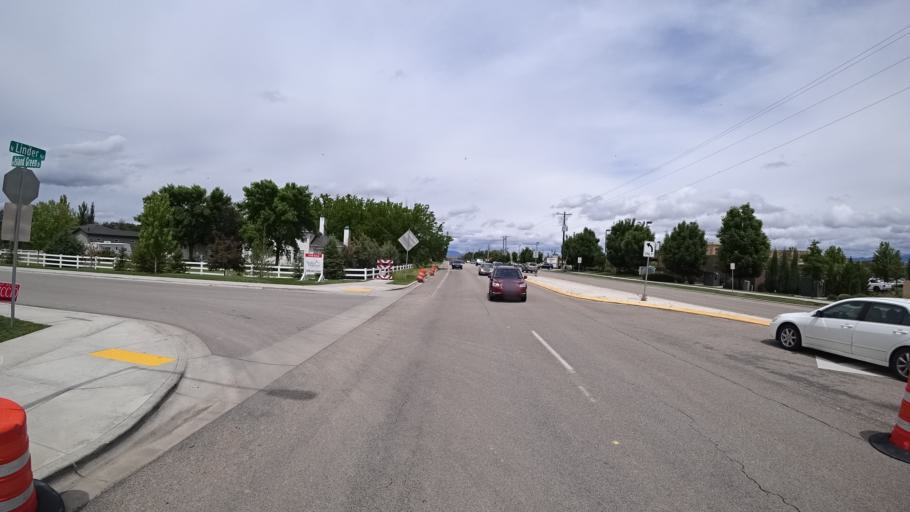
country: US
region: Idaho
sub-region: Ada County
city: Meridian
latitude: 43.6644
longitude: -116.4138
